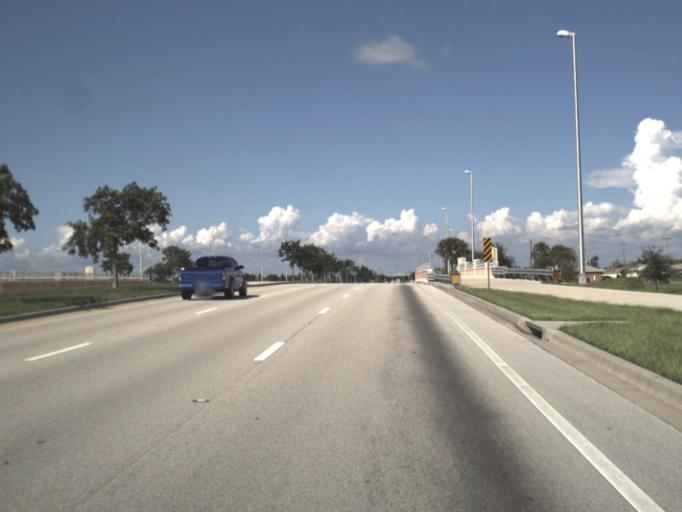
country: US
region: Florida
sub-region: Lee County
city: Lochmoor Waterway Estates
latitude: 26.6743
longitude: -81.9414
